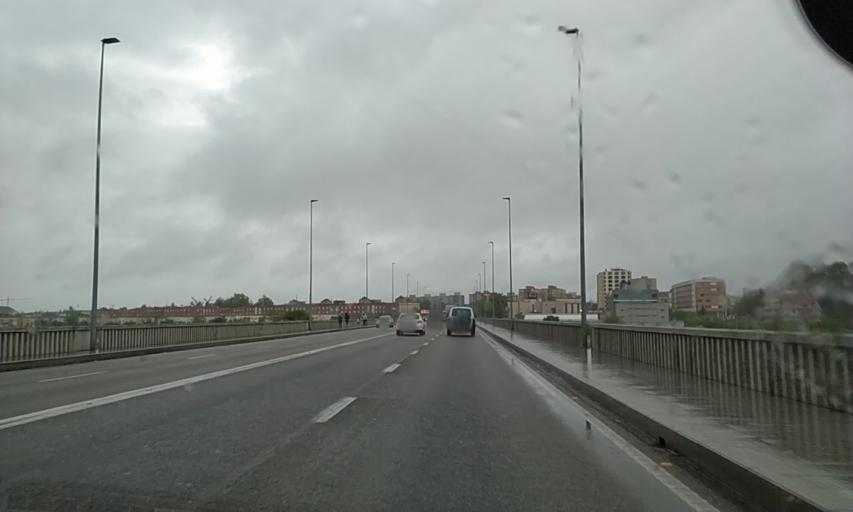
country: ES
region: Extremadura
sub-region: Provincia de Badajoz
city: Badajoz
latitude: 38.8799
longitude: -6.9819
